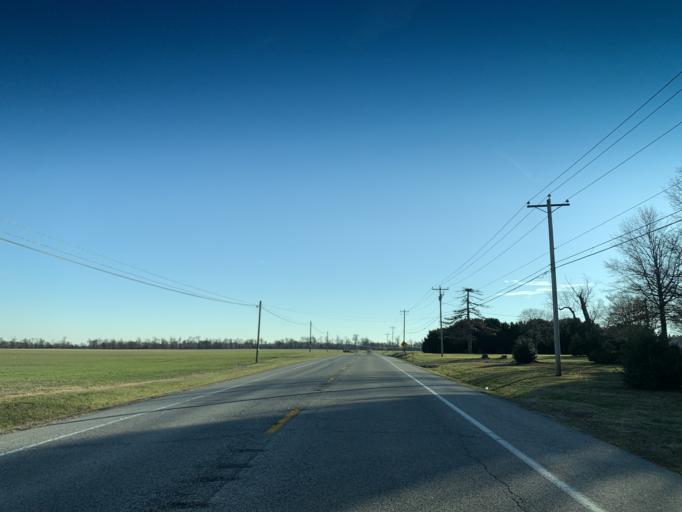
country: US
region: Delaware
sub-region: New Castle County
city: Middletown
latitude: 39.3929
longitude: -75.8711
